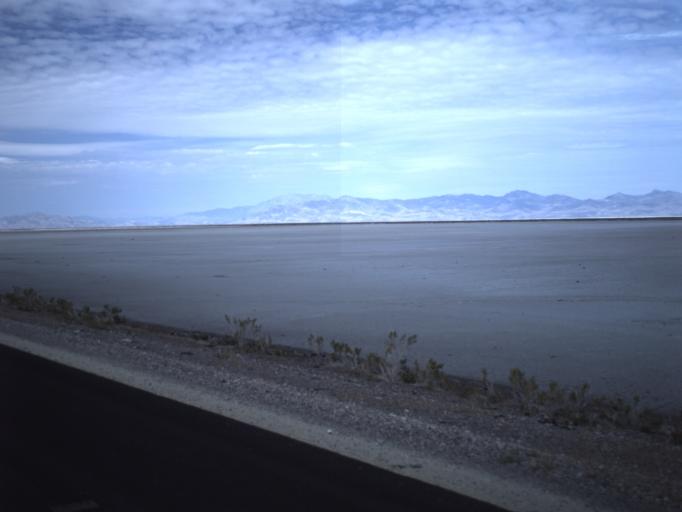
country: US
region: Utah
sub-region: Tooele County
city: Wendover
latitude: 40.7328
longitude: -113.5446
